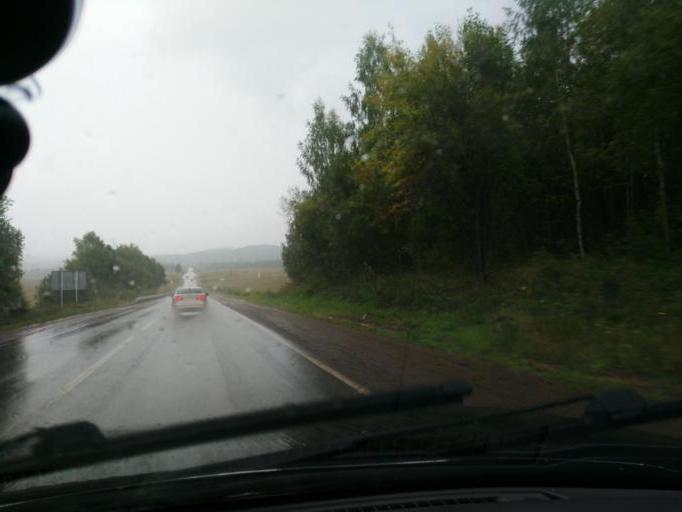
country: RU
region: Perm
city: Osa
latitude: 57.1803
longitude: 55.5448
